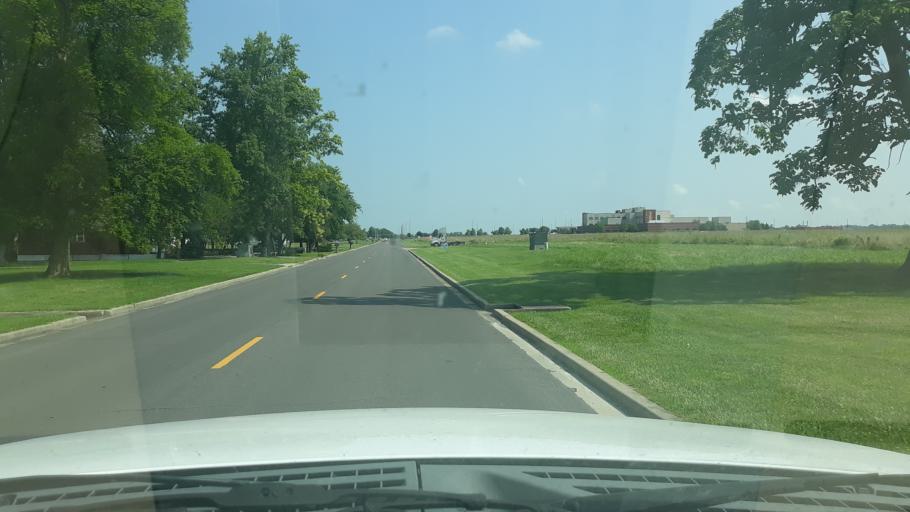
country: US
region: Illinois
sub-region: Williamson County
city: Energy
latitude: 37.7381
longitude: -88.9932
